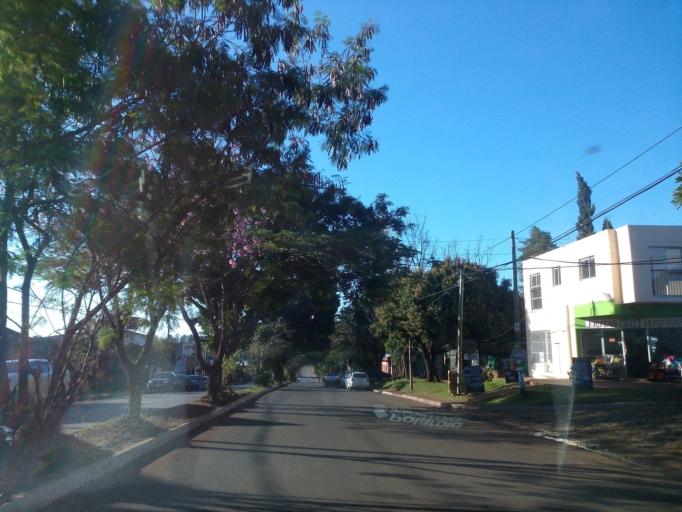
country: AR
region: Misiones
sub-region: Departamento de Capital
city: Posadas
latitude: -27.3966
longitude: -55.9362
